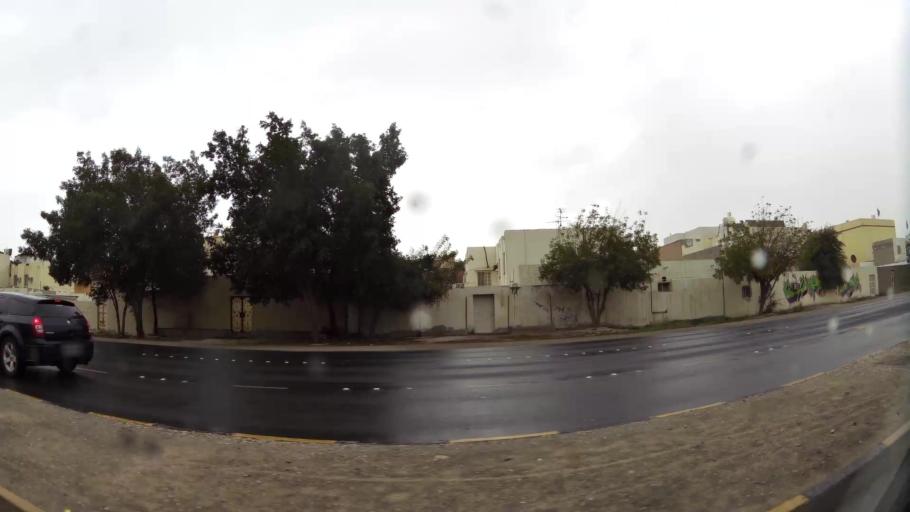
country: BH
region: Northern
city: Ar Rifa'
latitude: 26.1381
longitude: 50.5671
